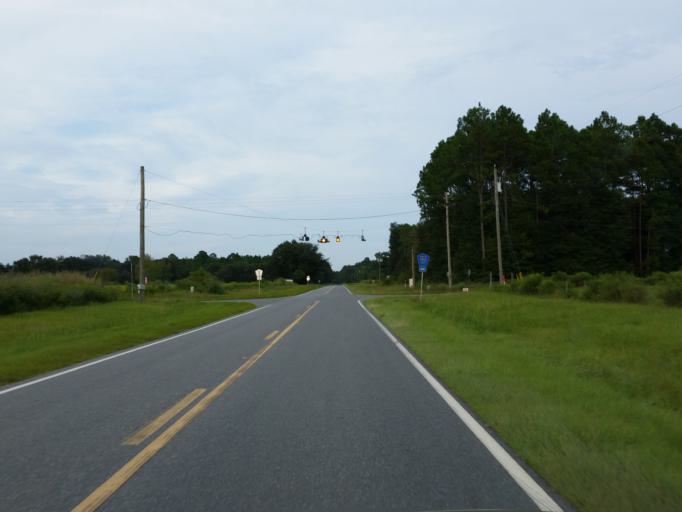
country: US
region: Georgia
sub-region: Echols County
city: Statenville
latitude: 30.5688
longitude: -83.1603
